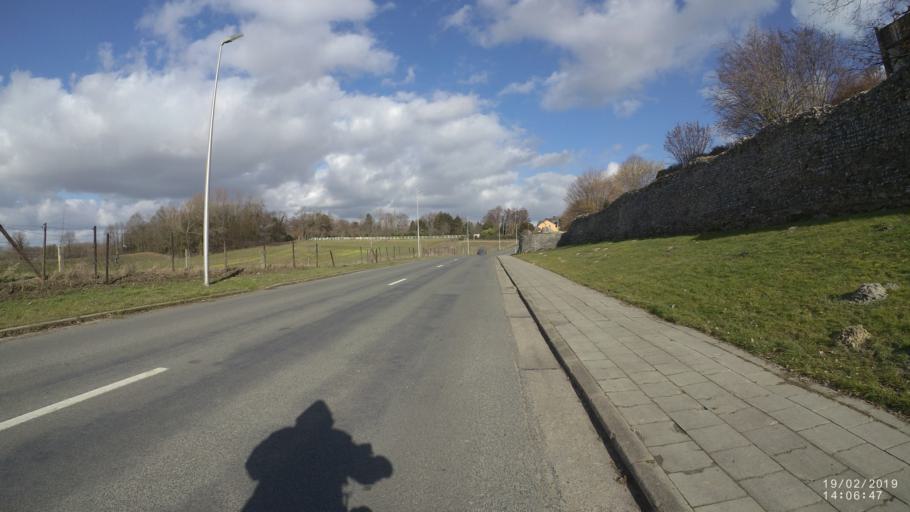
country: BE
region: Flanders
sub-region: Provincie Limburg
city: Tongeren
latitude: 50.7847
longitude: 5.4596
